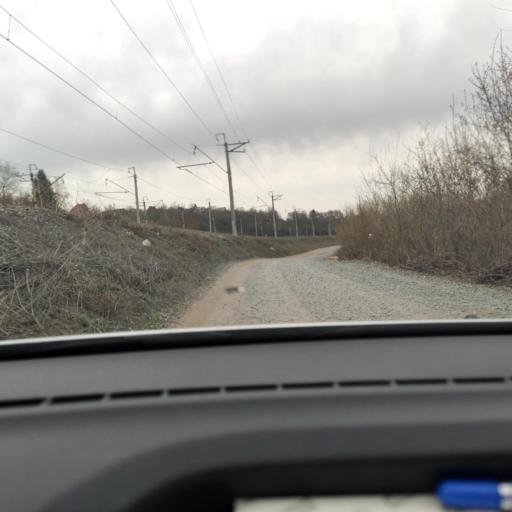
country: RU
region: Bashkortostan
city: Avdon
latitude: 54.6190
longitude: 55.6041
